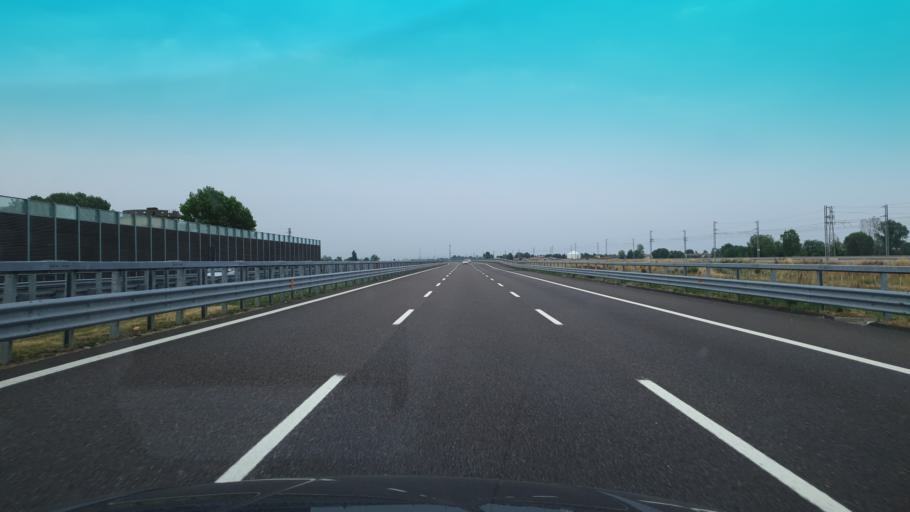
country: IT
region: Lombardy
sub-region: Provincia di Bergamo
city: Covo
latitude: 45.4888
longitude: 9.7723
